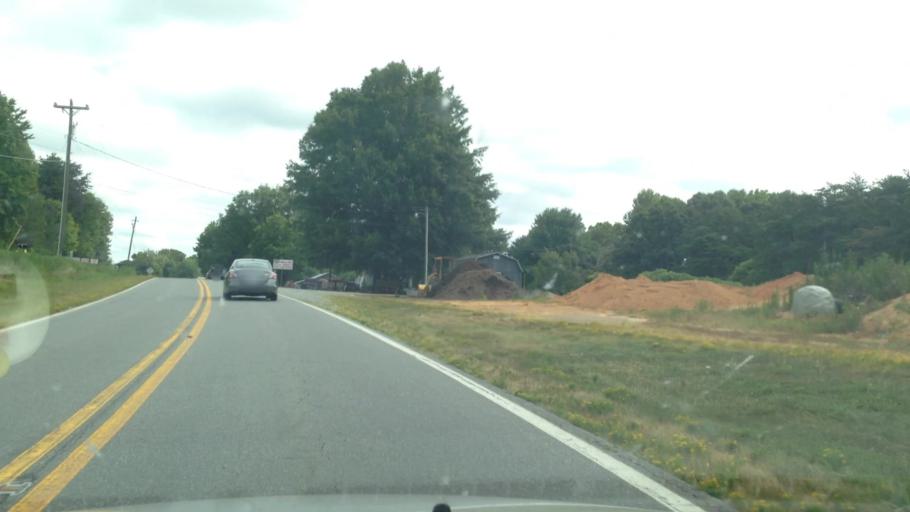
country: US
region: North Carolina
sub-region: Rockingham County
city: Reidsville
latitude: 36.3960
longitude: -79.6325
